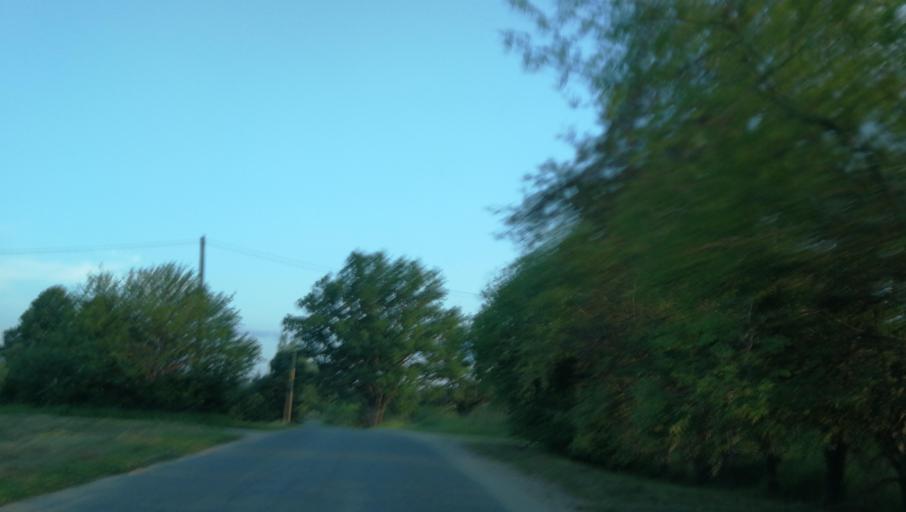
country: LV
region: Amatas Novads
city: Drabesi
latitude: 57.2478
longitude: 25.2147
